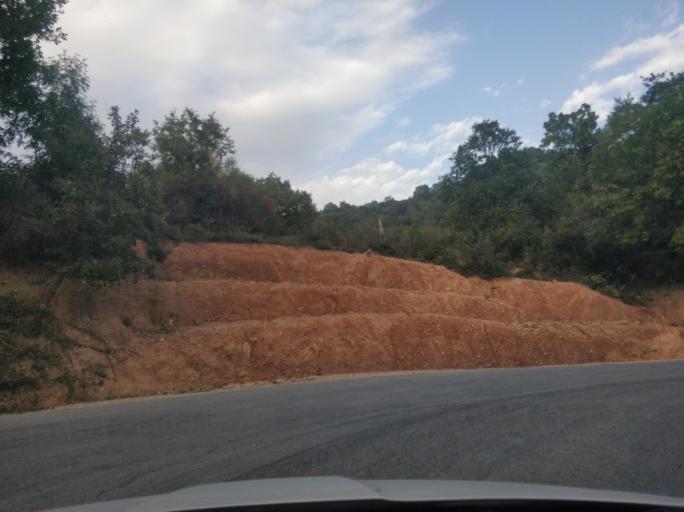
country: AL
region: Vlore
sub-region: Rrethi i Sarandes
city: Dhiver
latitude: 39.9173
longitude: 20.1991
